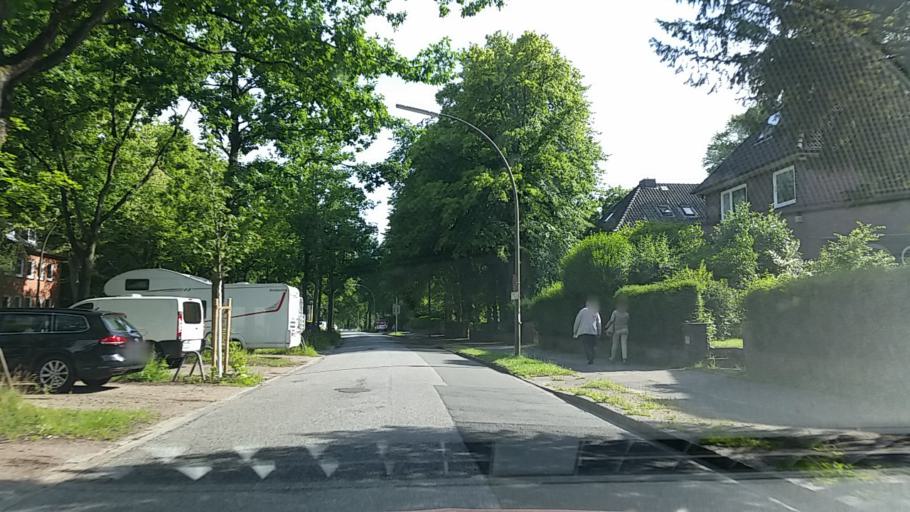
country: DE
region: Hamburg
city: Eidelstedt
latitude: 53.5643
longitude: 9.8871
